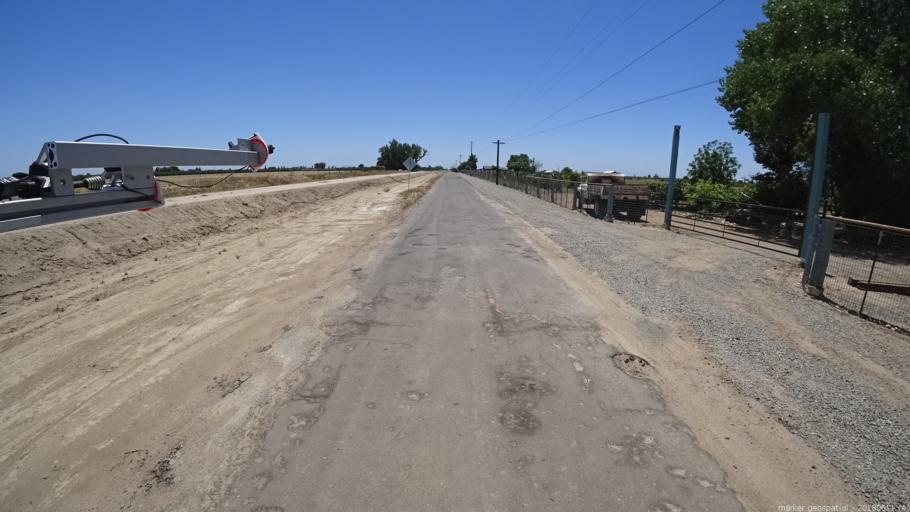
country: US
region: California
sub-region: Madera County
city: Fairmead
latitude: 37.0167
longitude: -120.1932
